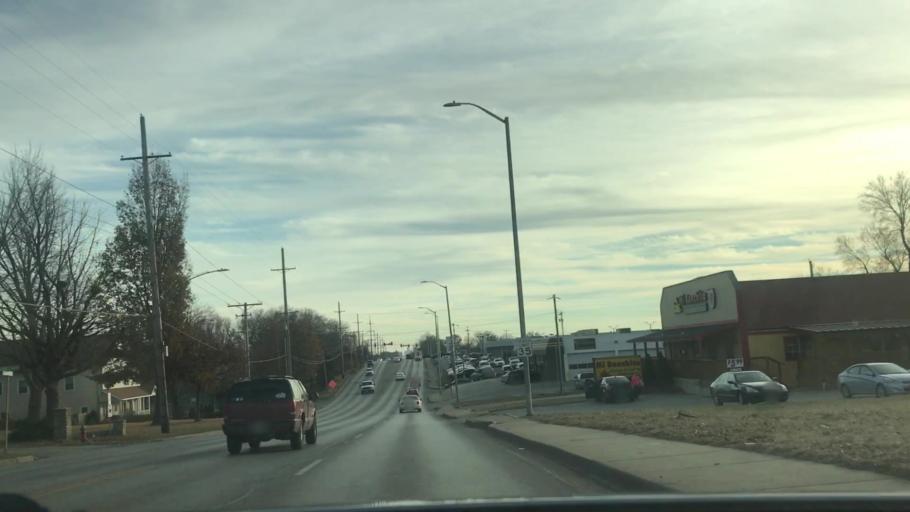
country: US
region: Missouri
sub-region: Clay County
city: Gladstone
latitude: 39.1987
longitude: -94.5765
